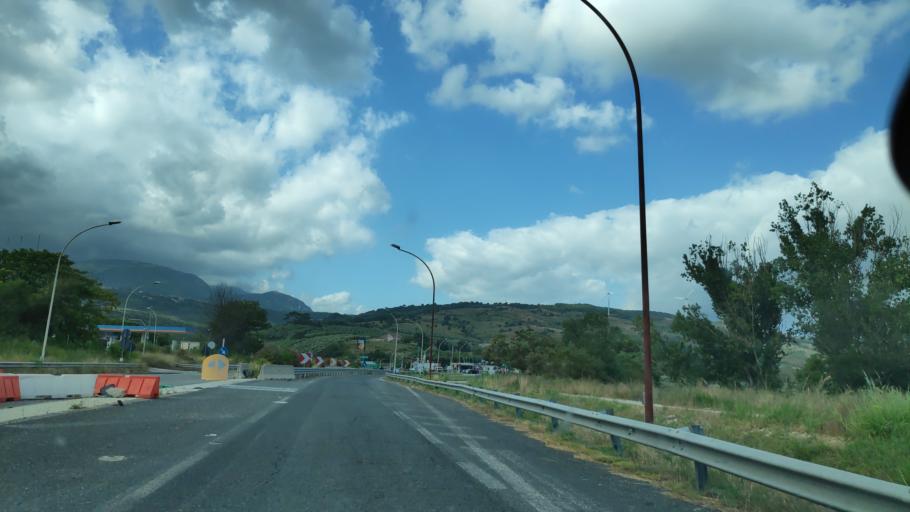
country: IT
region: Campania
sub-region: Provincia di Salerno
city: Serre
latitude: 40.6216
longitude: 15.1817
